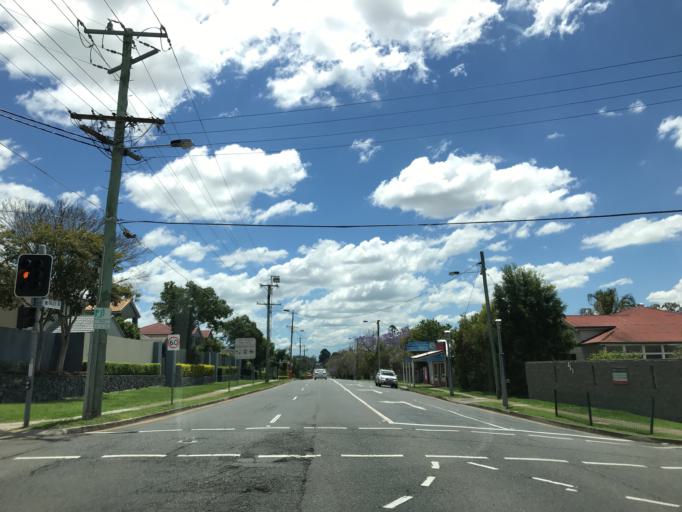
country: AU
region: Queensland
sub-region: Brisbane
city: Seventeen Mile Rocks
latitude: -27.5494
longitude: 152.9799
